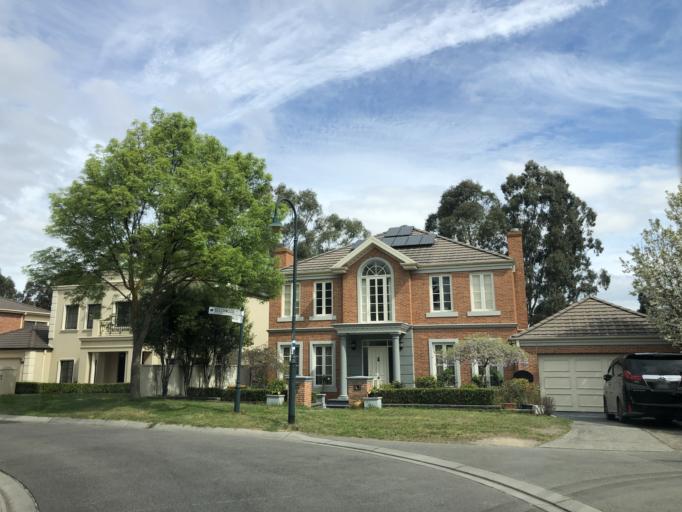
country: AU
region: Victoria
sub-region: Monash
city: Ashwood
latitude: -37.8648
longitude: 145.1021
